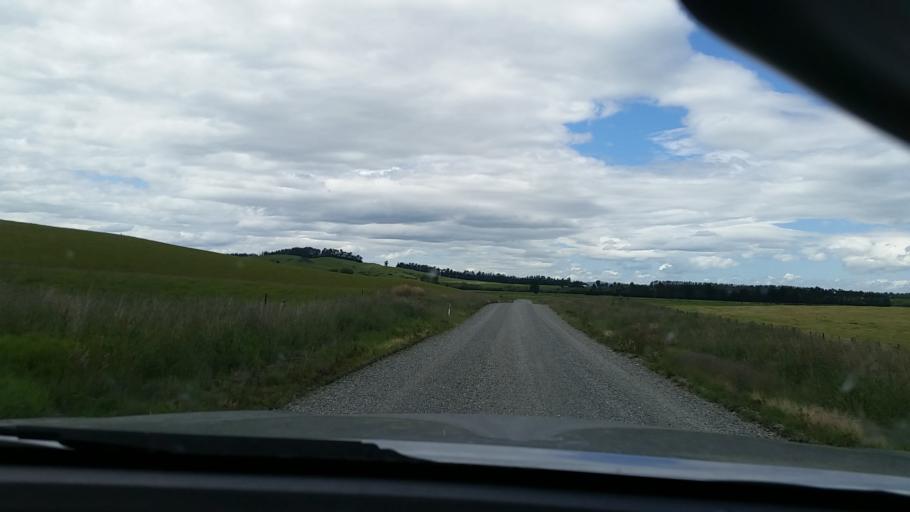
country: NZ
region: Otago
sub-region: Queenstown-Lakes District
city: Kingston
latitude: -45.7747
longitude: 168.6125
